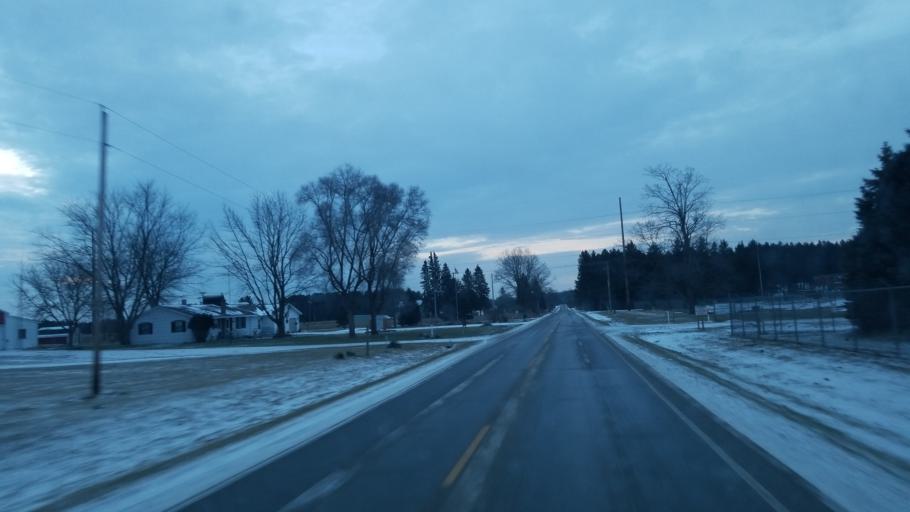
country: US
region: Michigan
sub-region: Osceola County
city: Reed City
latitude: 43.8389
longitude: -85.4242
